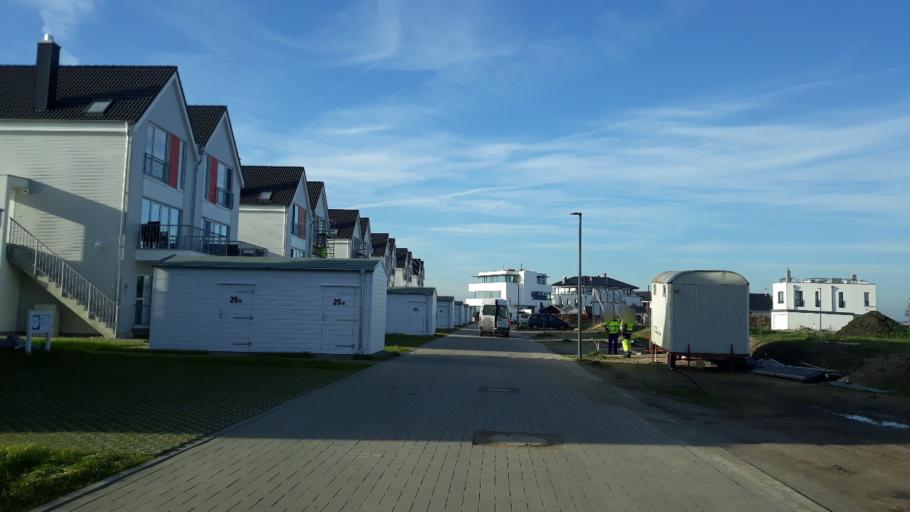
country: DE
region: Schleswig-Holstein
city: Maasholm
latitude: 54.6630
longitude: 10.0303
